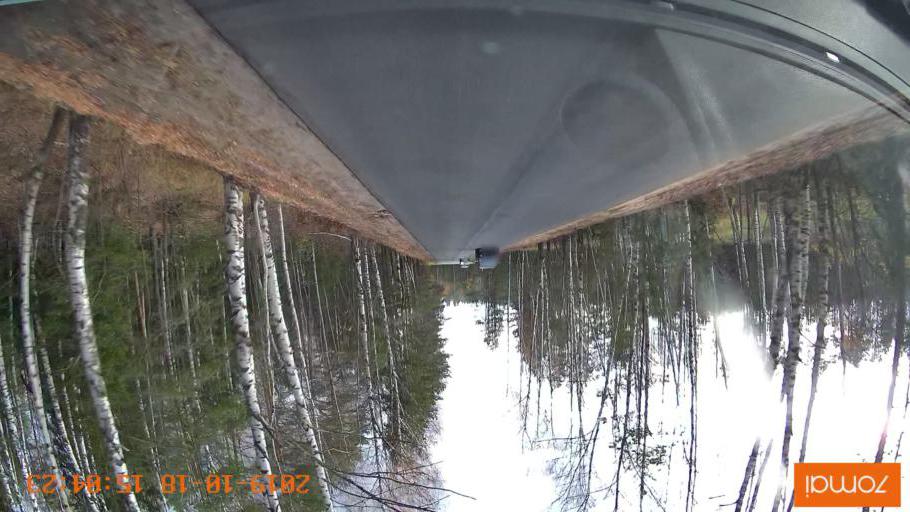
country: RU
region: Vladimir
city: Kurlovo
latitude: 55.5044
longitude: 40.5743
